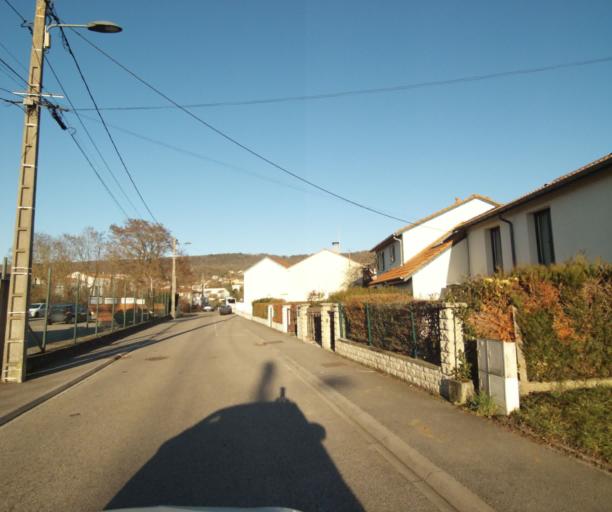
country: FR
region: Lorraine
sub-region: Departement de Meurthe-et-Moselle
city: Malzeville
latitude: 48.7128
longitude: 6.1804
